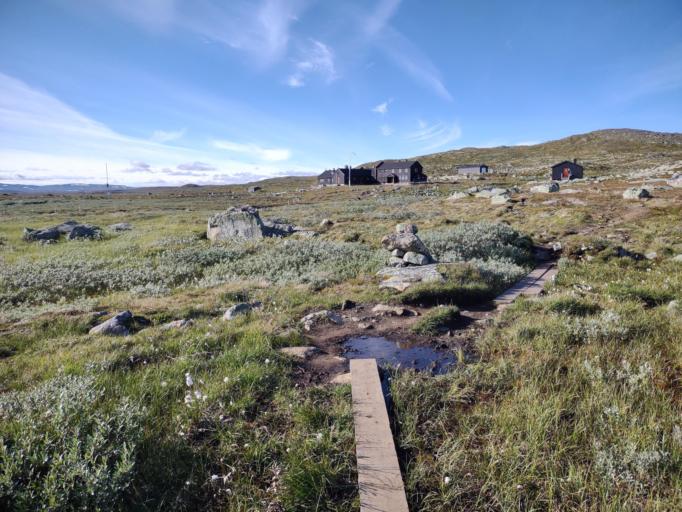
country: NO
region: Hordaland
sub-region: Eidfjord
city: Eidfjord
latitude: 60.1822
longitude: 7.4827
